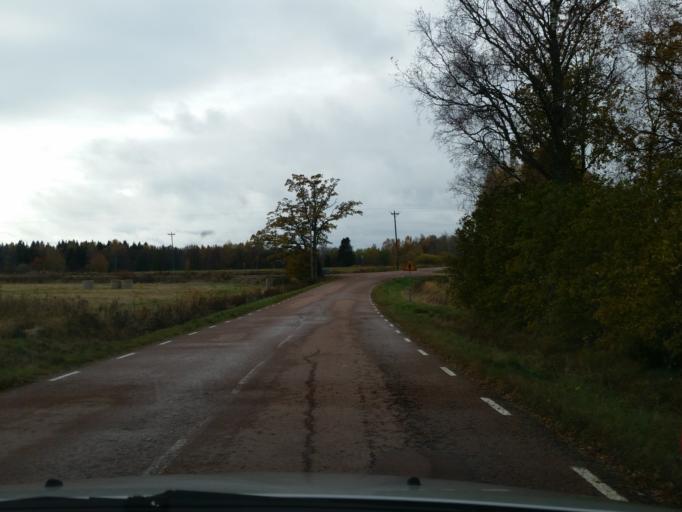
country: AX
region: Alands landsbygd
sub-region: Lemland
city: Lemland
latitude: 60.0245
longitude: 20.1634
